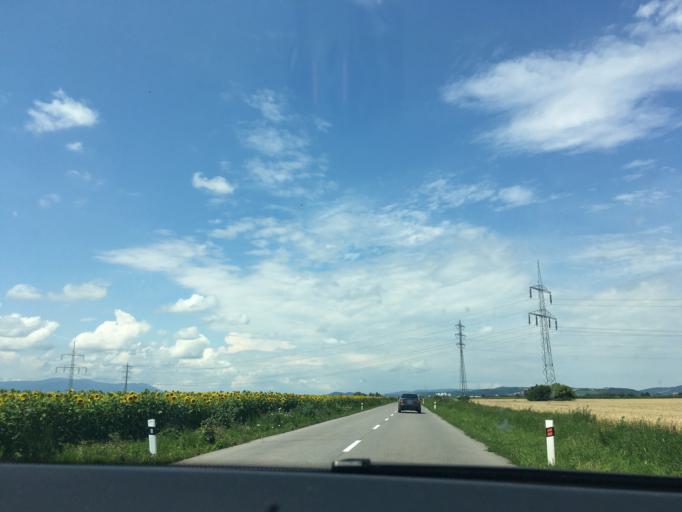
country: SK
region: Presovsky
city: Vranov nad Topl'ou
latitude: 48.8266
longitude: 21.7232
